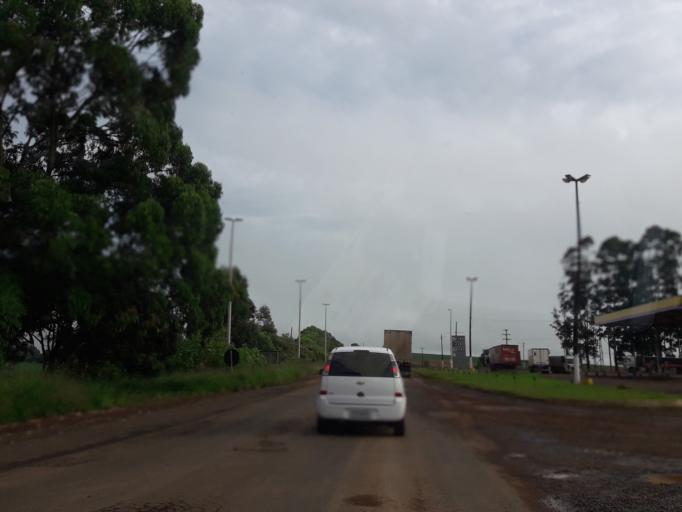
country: AR
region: Misiones
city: Bernardo de Irigoyen
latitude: -26.3124
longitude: -53.5477
